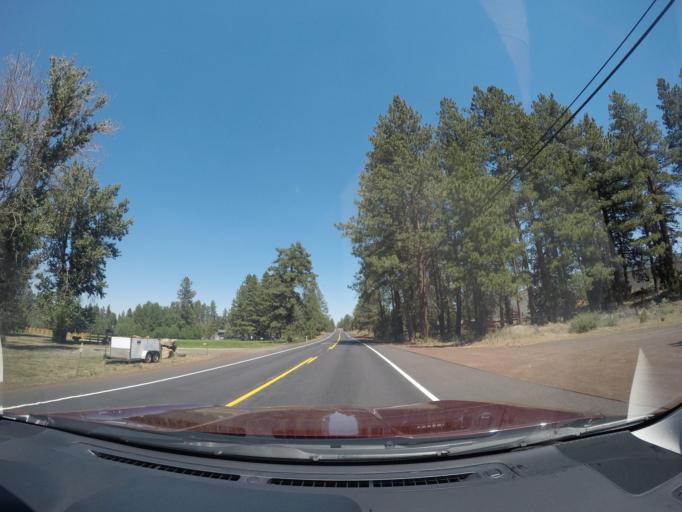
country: US
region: Oregon
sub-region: Deschutes County
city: Sisters
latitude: 44.2867
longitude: -121.5131
